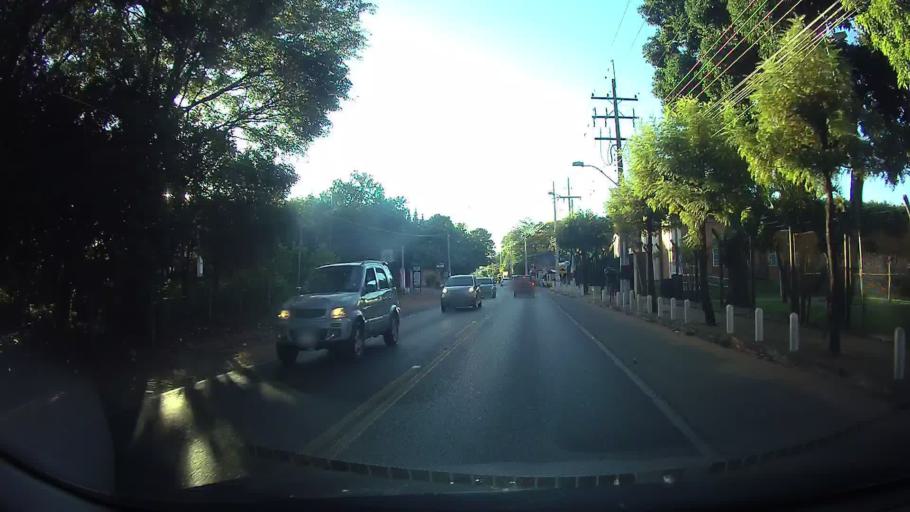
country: PY
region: Central
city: Aregua
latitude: -25.2978
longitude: -57.4146
